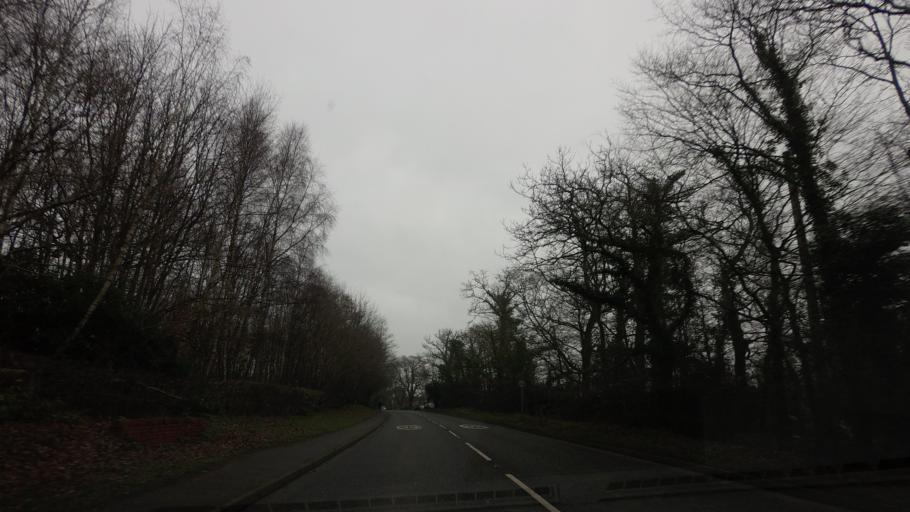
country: GB
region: England
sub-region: Kent
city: Cranbrook
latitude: 51.1028
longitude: 0.5356
